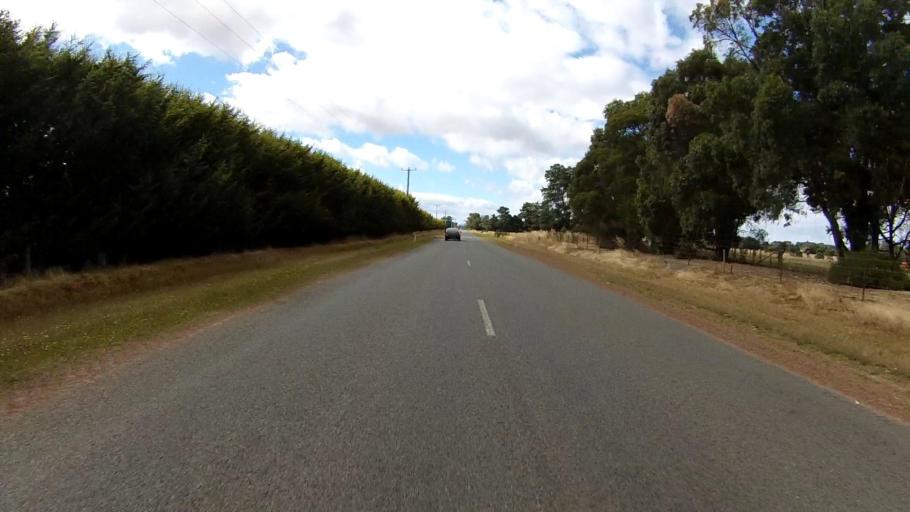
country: AU
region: Tasmania
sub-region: Northern Midlands
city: Evandale
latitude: -41.6079
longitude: 147.2846
